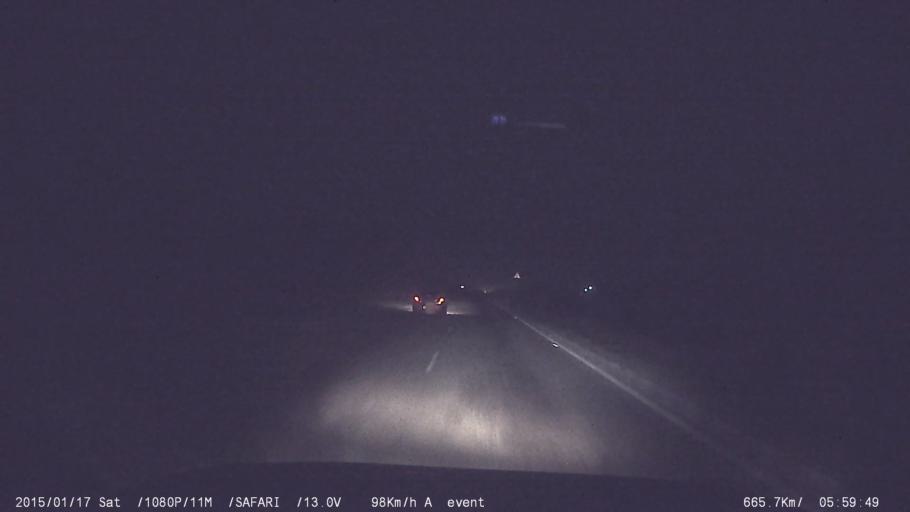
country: IN
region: Tamil Nadu
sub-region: Kancheepuram
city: Kanchipuram
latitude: 12.8971
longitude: 79.5708
